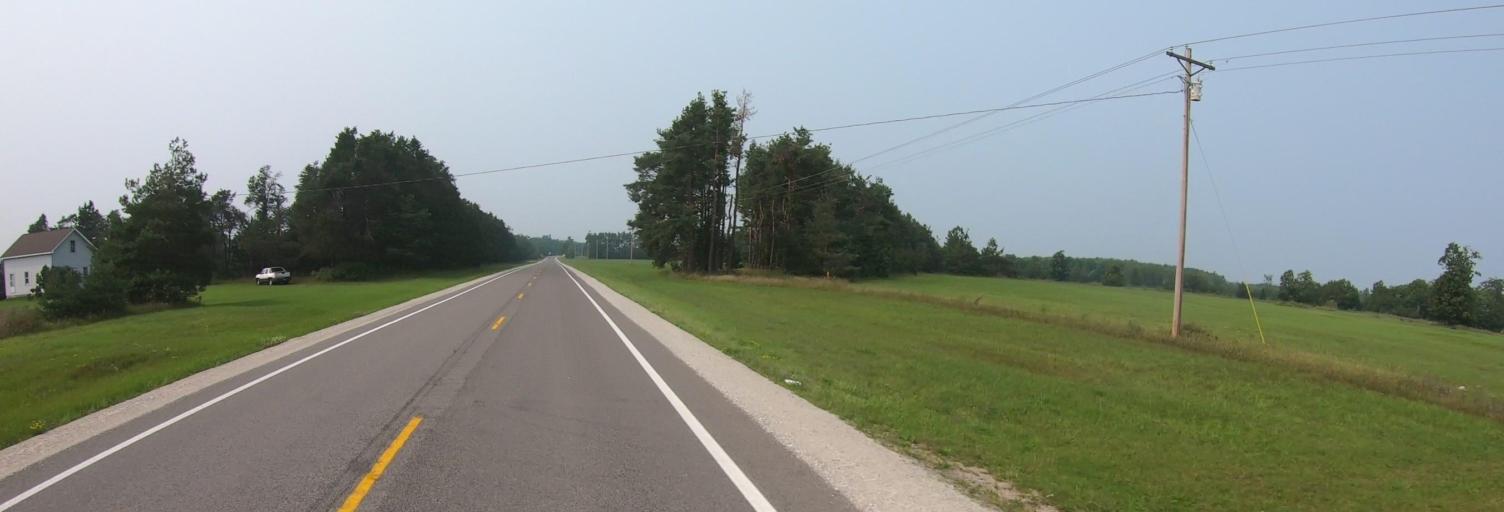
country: US
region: Michigan
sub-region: Chippewa County
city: Sault Ste. Marie
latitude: 46.0358
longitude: -84.0871
